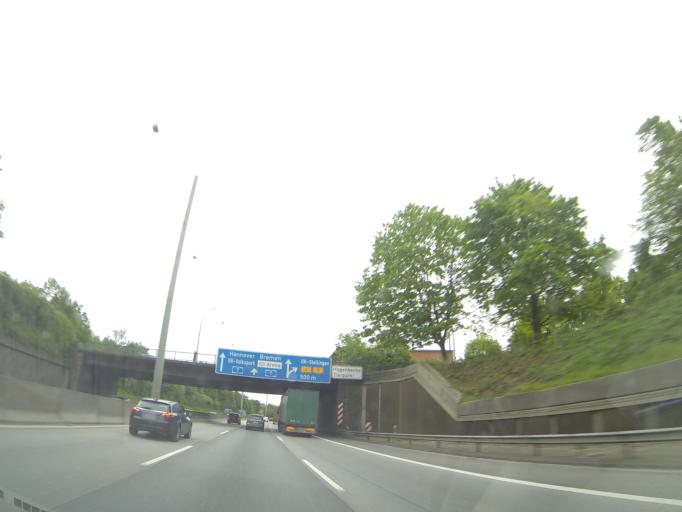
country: DE
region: Hamburg
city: Stellingen
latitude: 53.6005
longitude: 9.9223
